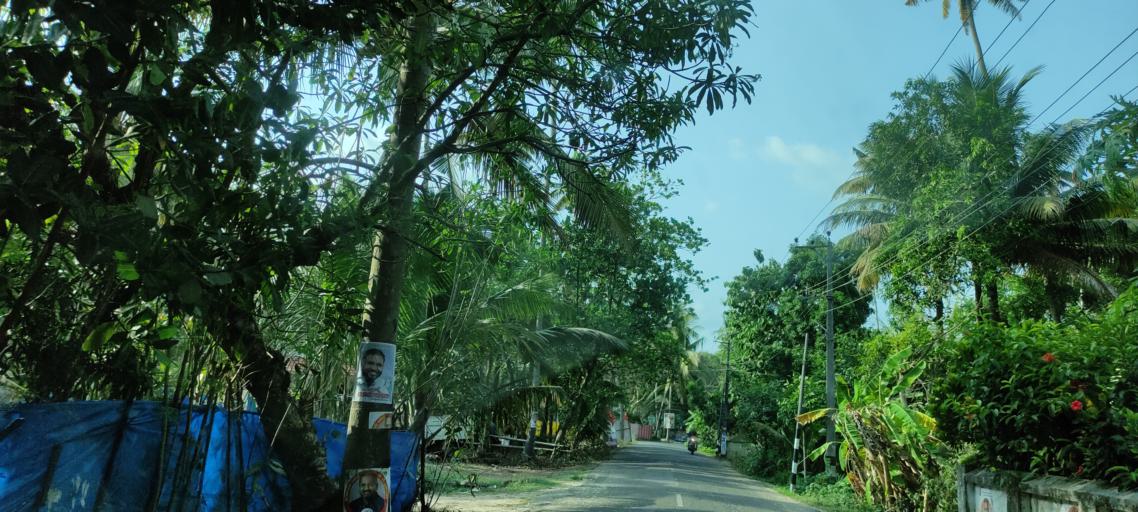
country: IN
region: Kerala
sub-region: Alappuzha
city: Vayalar
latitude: 9.7163
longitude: 76.2878
